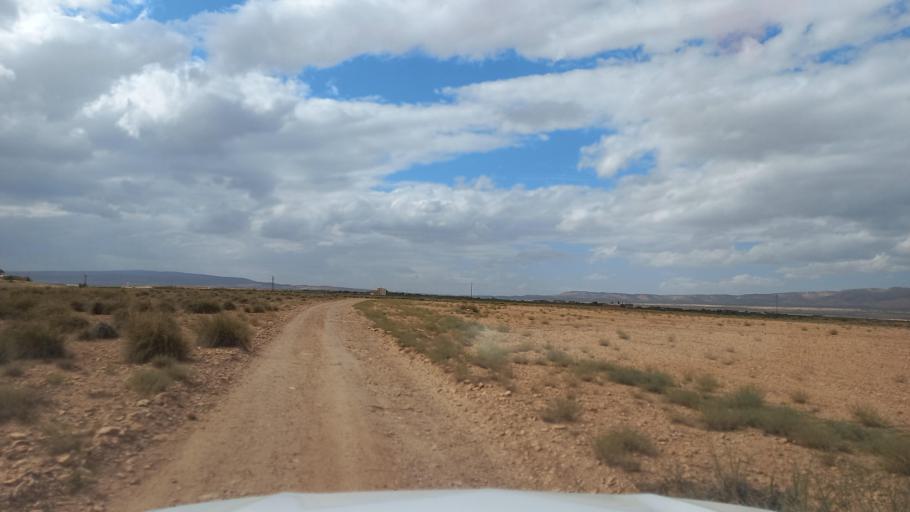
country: TN
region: Al Qasrayn
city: Sbiba
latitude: 35.3798
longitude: 9.1023
